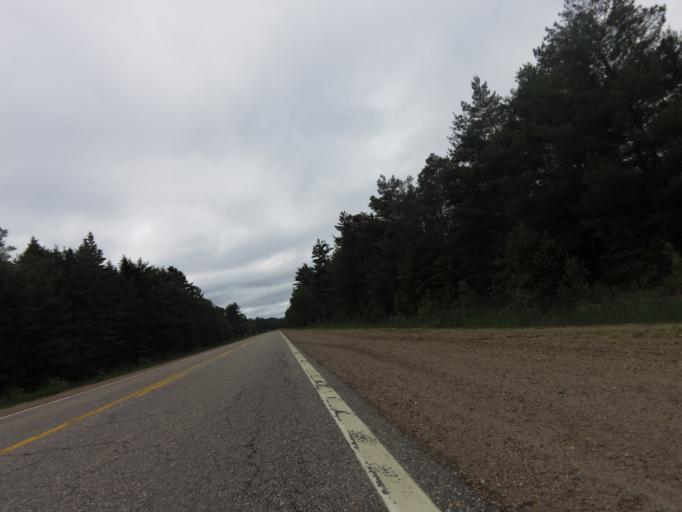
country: CA
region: Quebec
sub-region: Outaouais
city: Shawville
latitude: 45.8683
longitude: -76.4059
